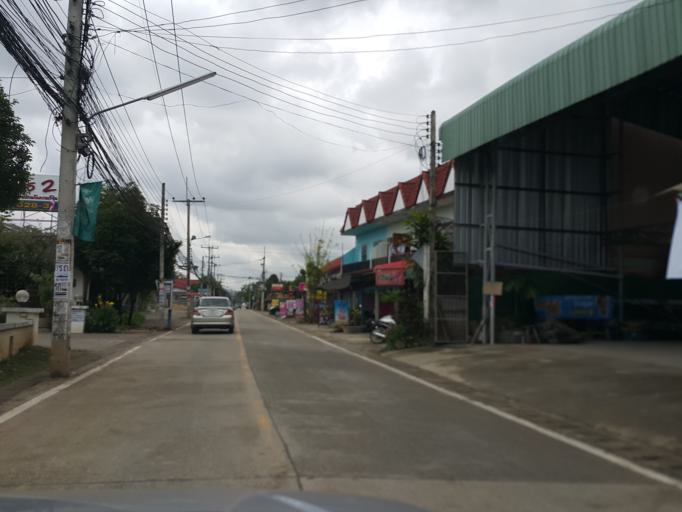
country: TH
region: Lamphun
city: Lamphun
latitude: 18.5760
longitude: 99.0701
